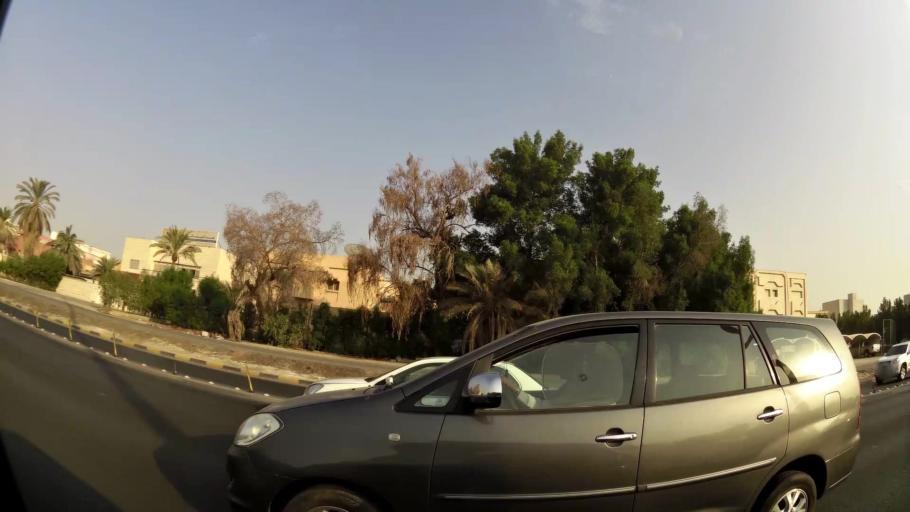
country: KW
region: Muhafazat Hawalli
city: Hawalli
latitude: 29.3221
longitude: 48.0061
